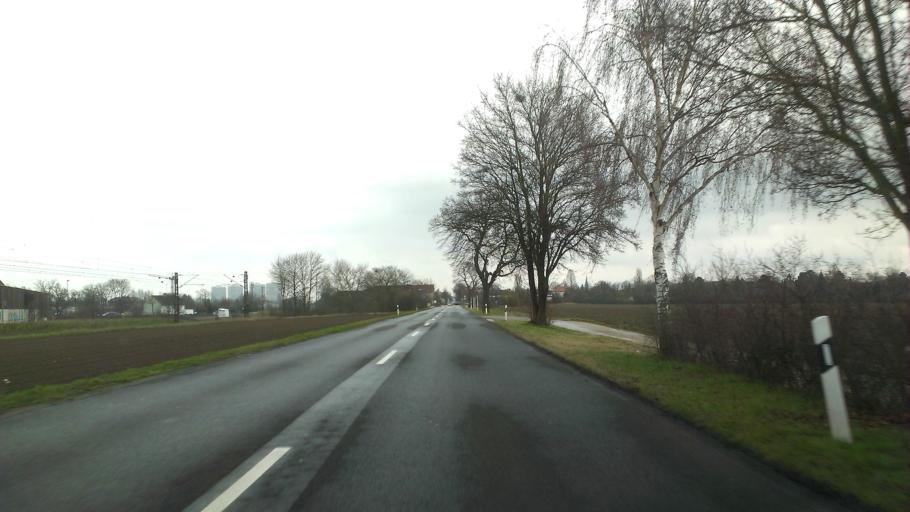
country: DE
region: Rheinland-Pfalz
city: Frankenthal
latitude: 49.5004
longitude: 8.3624
